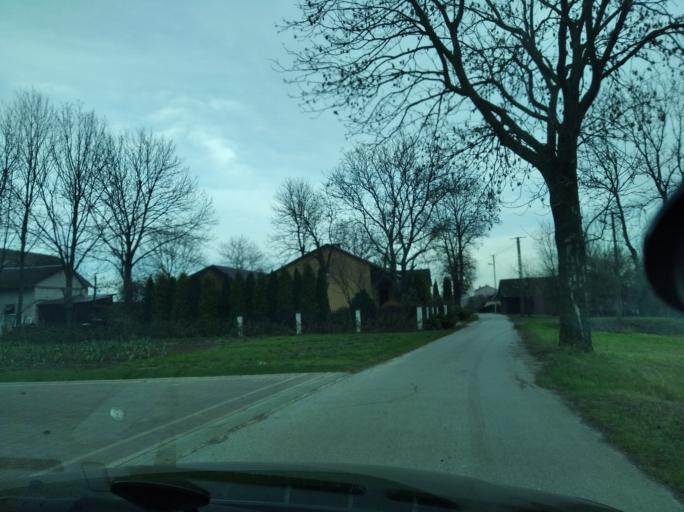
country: PL
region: Subcarpathian Voivodeship
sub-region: Powiat przeworski
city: Debow
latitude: 50.0495
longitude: 22.4278
